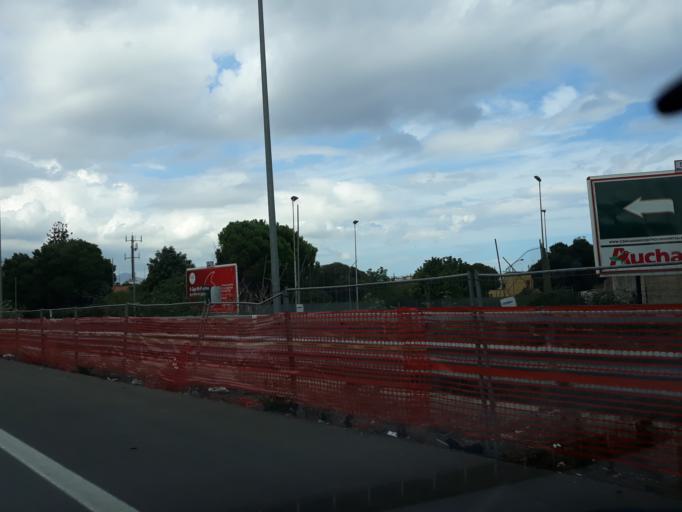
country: IT
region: Sicily
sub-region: Palermo
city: Ciaculli
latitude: 38.0873
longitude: 13.3971
